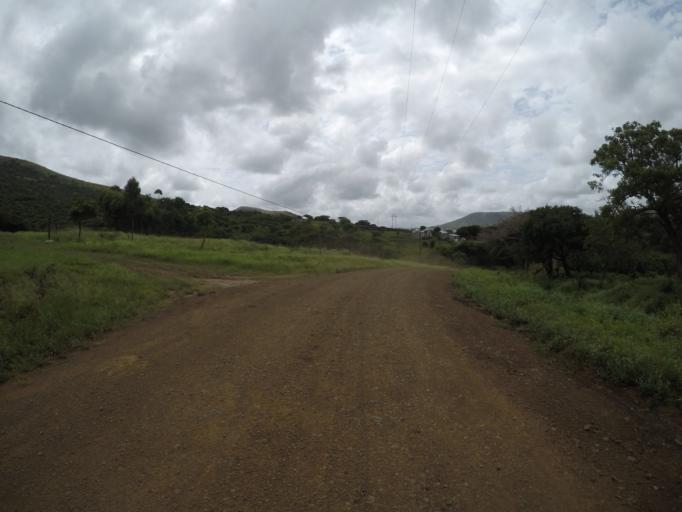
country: ZA
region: KwaZulu-Natal
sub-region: uThungulu District Municipality
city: Empangeni
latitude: -28.5919
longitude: 31.8833
